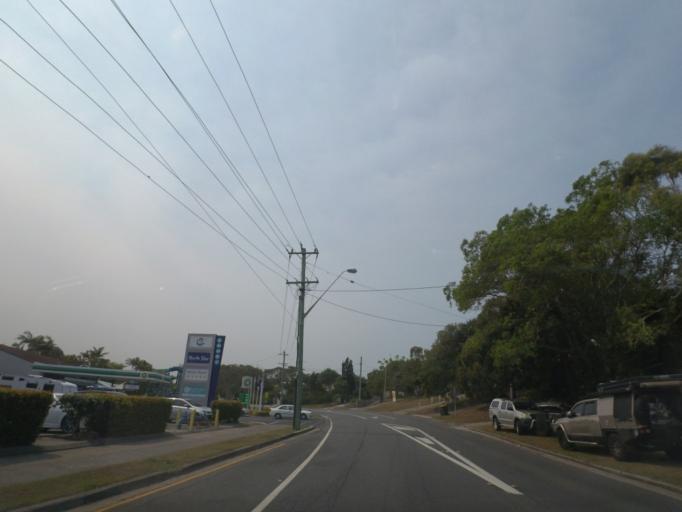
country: AU
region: New South Wales
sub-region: Tweed
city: Pottsville Beach
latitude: -28.3561
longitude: 153.5734
